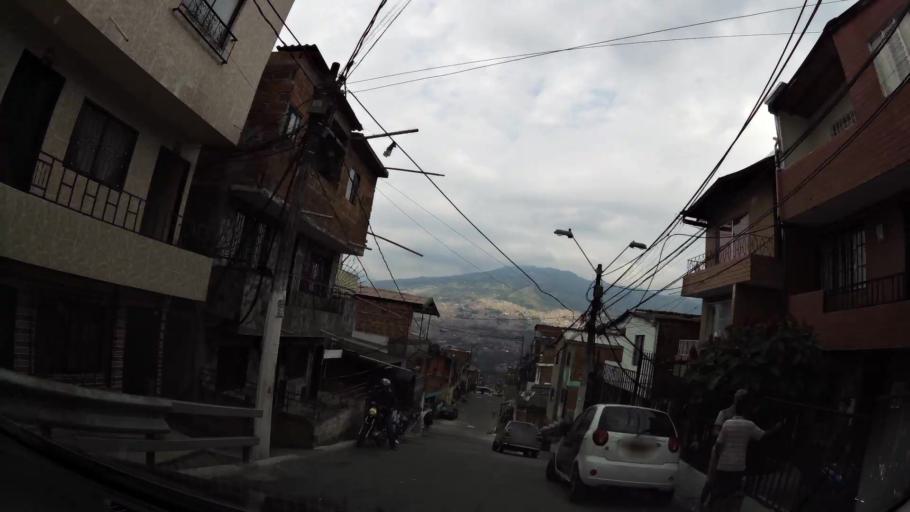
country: CO
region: Antioquia
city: Medellin
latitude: 6.2908
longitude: -75.5525
